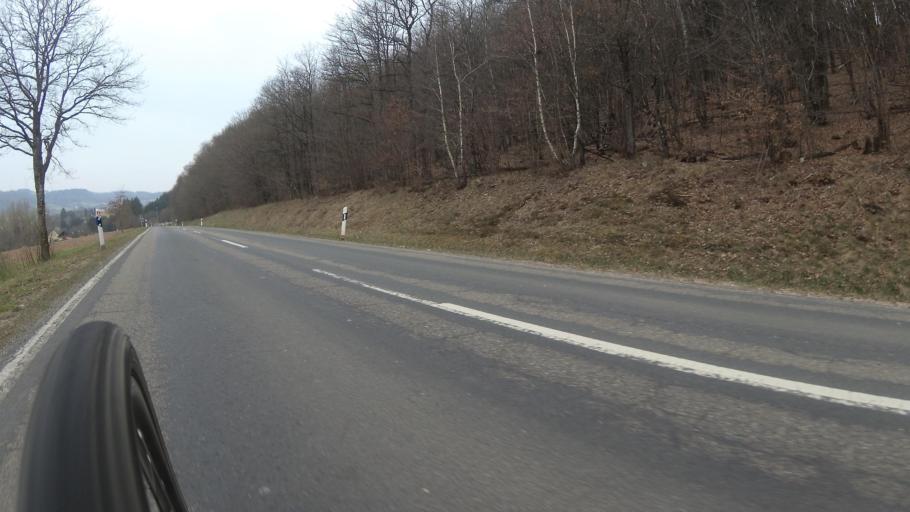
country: DE
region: Rheinland-Pfalz
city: Dienstweiler
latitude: 49.6291
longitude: 7.1933
